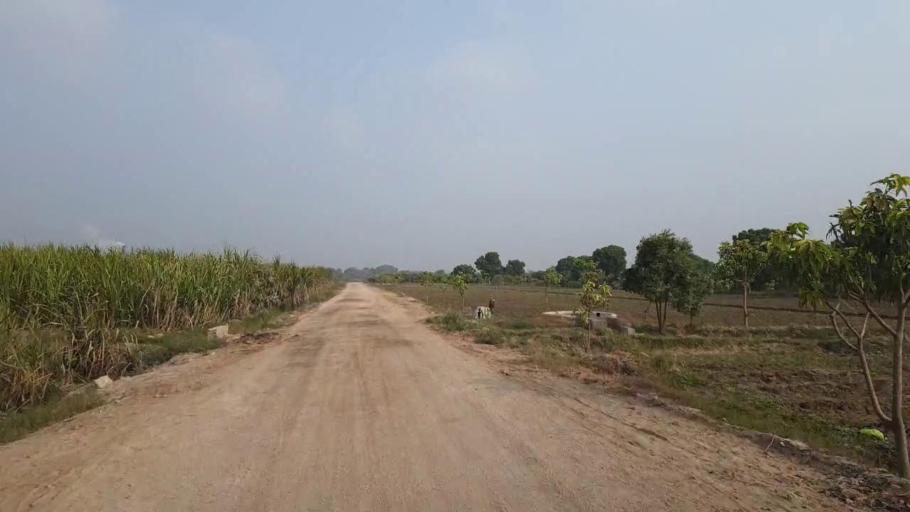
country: PK
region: Sindh
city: Tando Muhammad Khan
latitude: 25.1634
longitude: 68.5934
